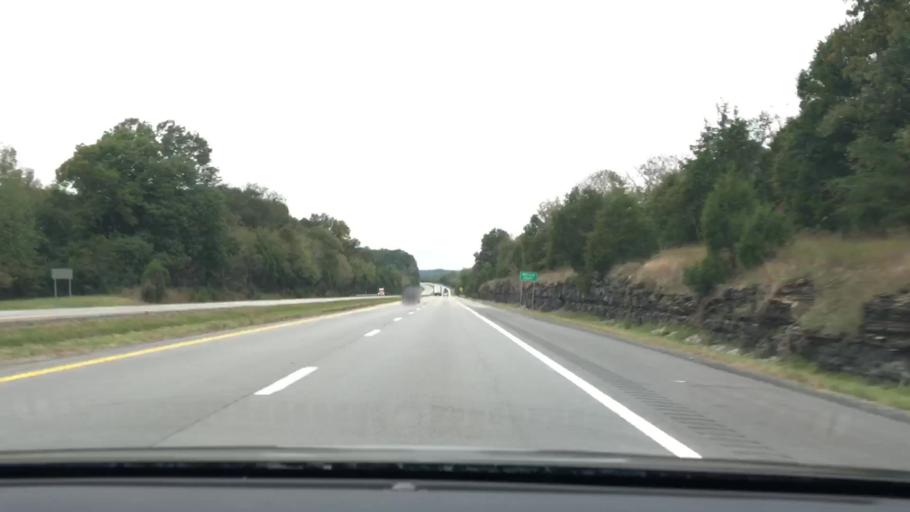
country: US
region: Kentucky
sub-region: Metcalfe County
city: Edmonton
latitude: 37.0278
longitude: -85.5093
